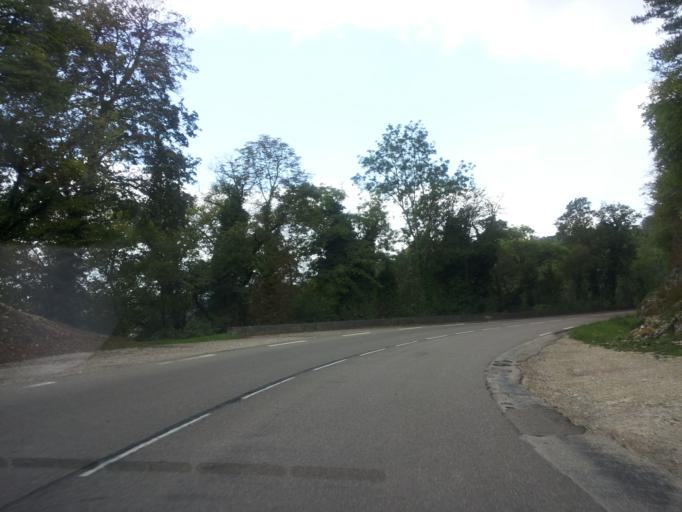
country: FR
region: Lorraine
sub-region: Departement des Vosges
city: Neufchateau
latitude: 48.3532
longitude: 5.7161
